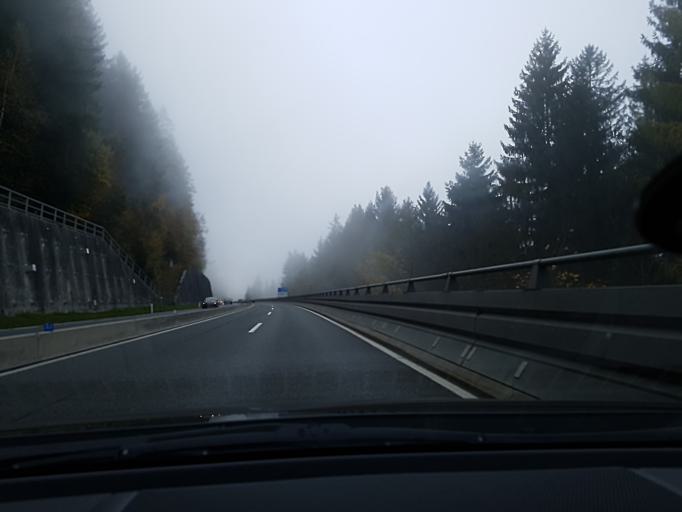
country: AT
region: Salzburg
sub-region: Politischer Bezirk Sankt Johann im Pongau
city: Bischofshofen
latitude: 47.4102
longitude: 13.2238
